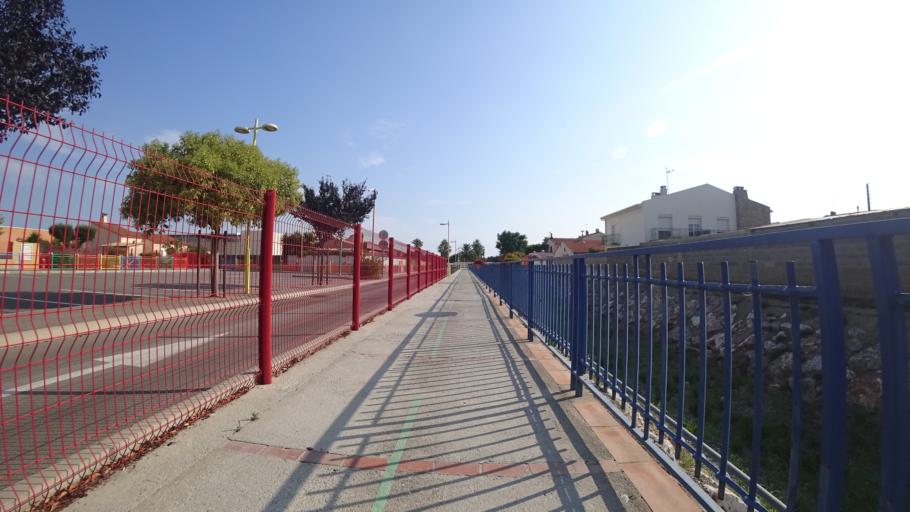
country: FR
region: Languedoc-Roussillon
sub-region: Departement des Pyrenees-Orientales
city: Claira
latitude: 42.7607
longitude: 2.9535
